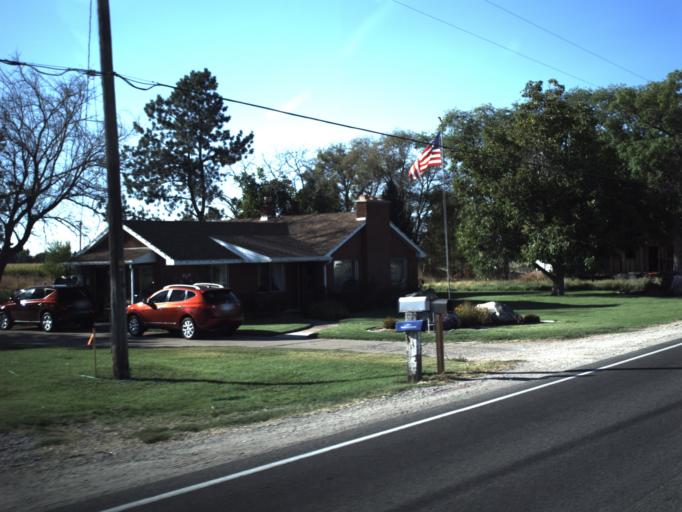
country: US
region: Utah
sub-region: Weber County
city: Hooper
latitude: 41.1762
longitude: -112.1226
